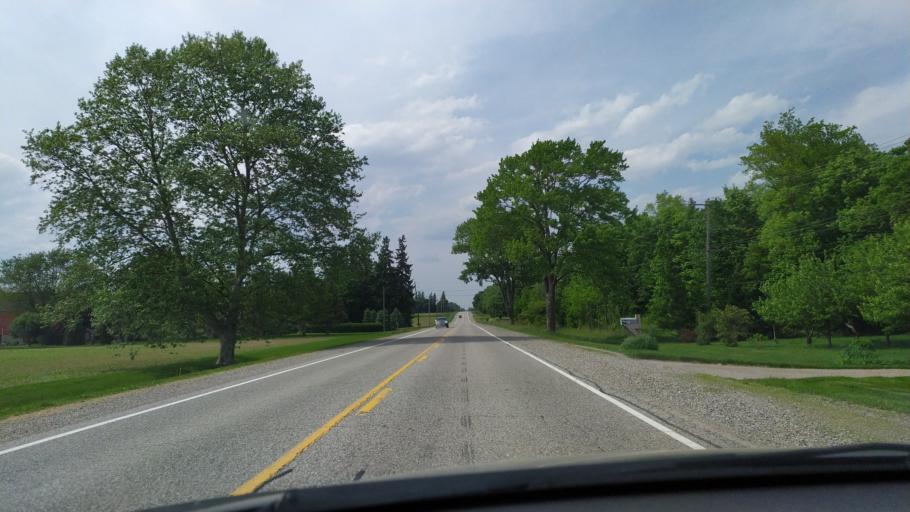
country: CA
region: Ontario
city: Dorchester
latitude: 43.0925
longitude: -81.0064
